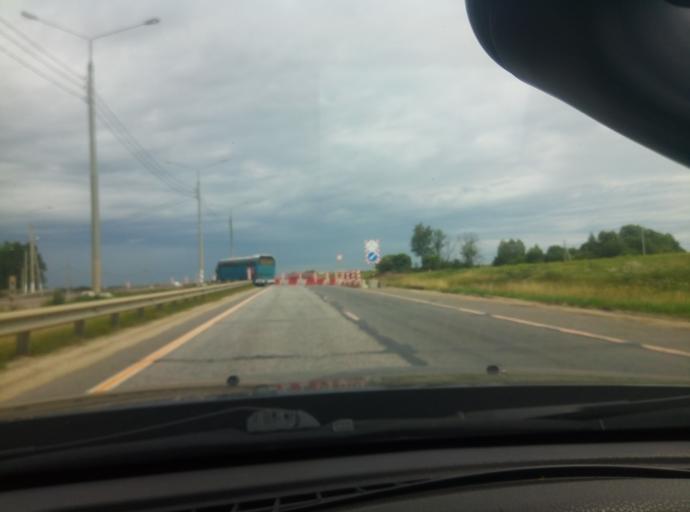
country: RU
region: Tula
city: Leninskiy
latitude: 54.4329
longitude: 37.5069
